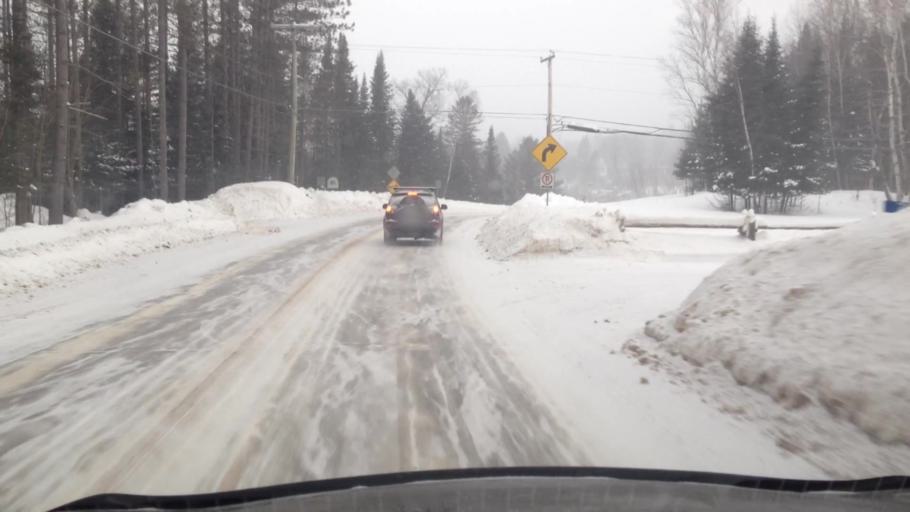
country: CA
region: Quebec
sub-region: Laurentides
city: Mont-Tremblant
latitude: 45.9728
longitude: -74.6305
